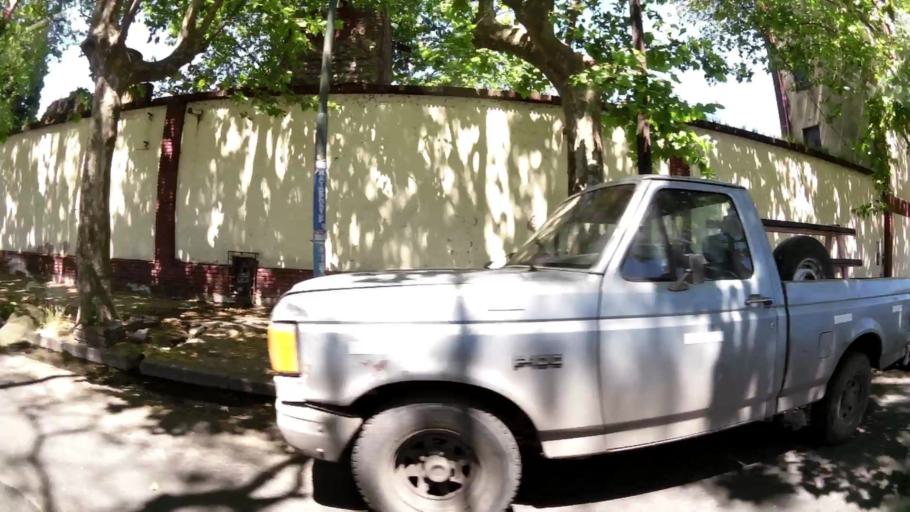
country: AR
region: Buenos Aires
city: Caseros
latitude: -34.5846
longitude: -58.5502
